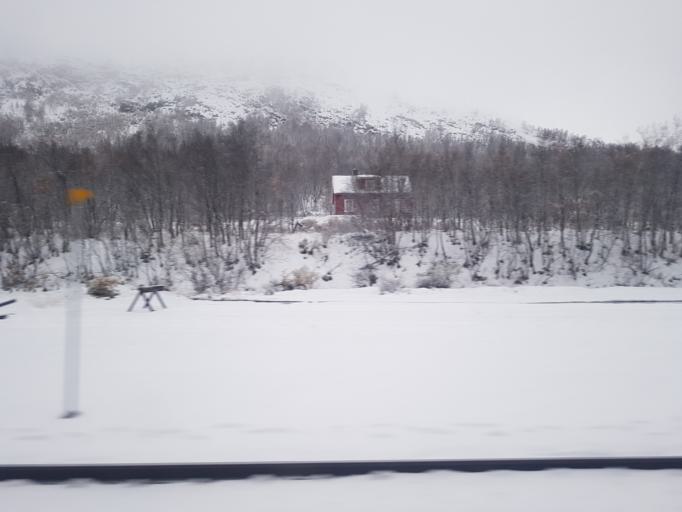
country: NO
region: Oppland
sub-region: Dovre
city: Dovre
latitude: 62.2242
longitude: 9.5503
